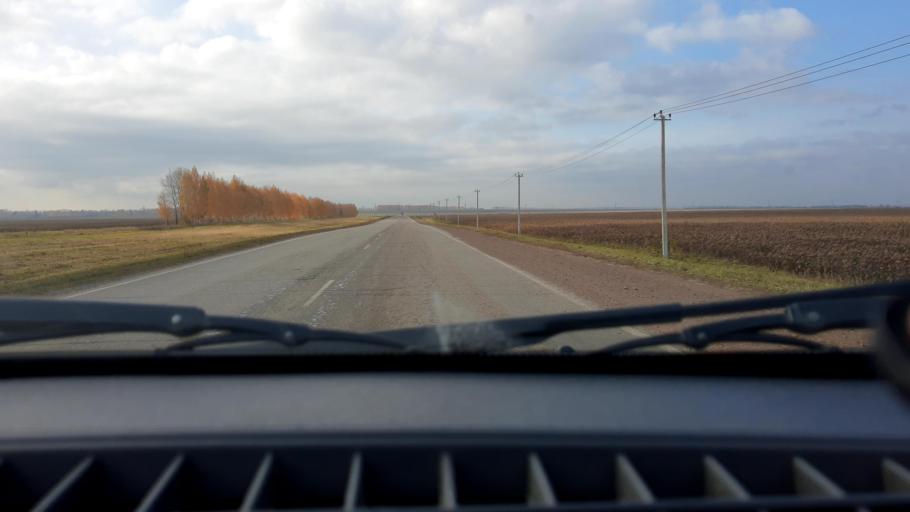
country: RU
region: Bashkortostan
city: Kabakovo
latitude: 54.5455
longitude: 56.0827
